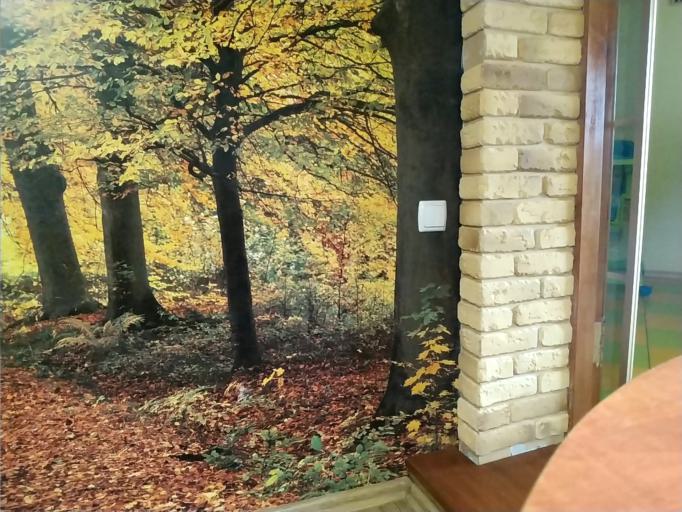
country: RU
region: Smolensk
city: Dorogobuzh
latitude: 54.8861
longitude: 33.3085
